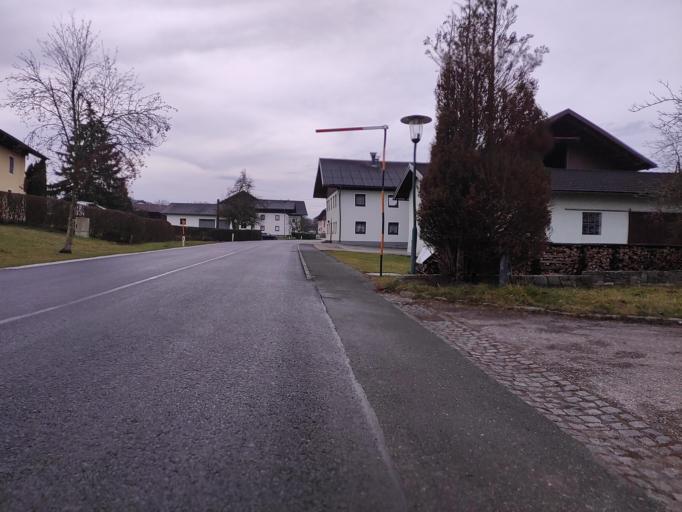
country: AT
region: Salzburg
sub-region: Politischer Bezirk Salzburg-Umgebung
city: Berndorf bei Salzburg
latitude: 47.9979
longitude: 13.0661
